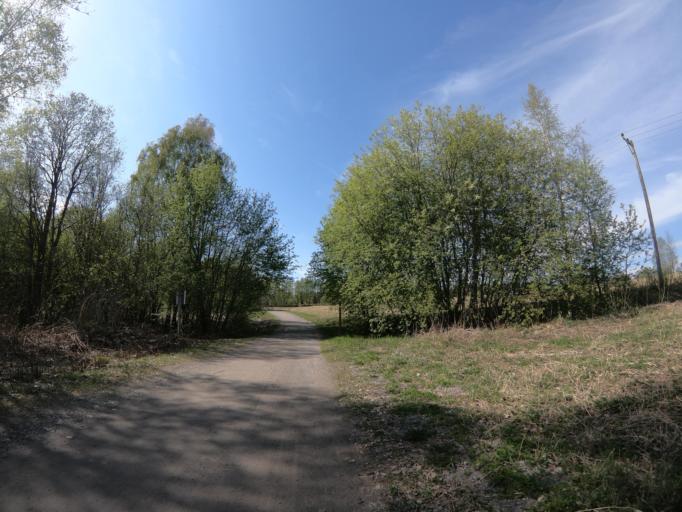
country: SE
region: Vaesterbotten
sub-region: Umea Kommun
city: Roback
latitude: 63.8294
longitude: 20.1812
